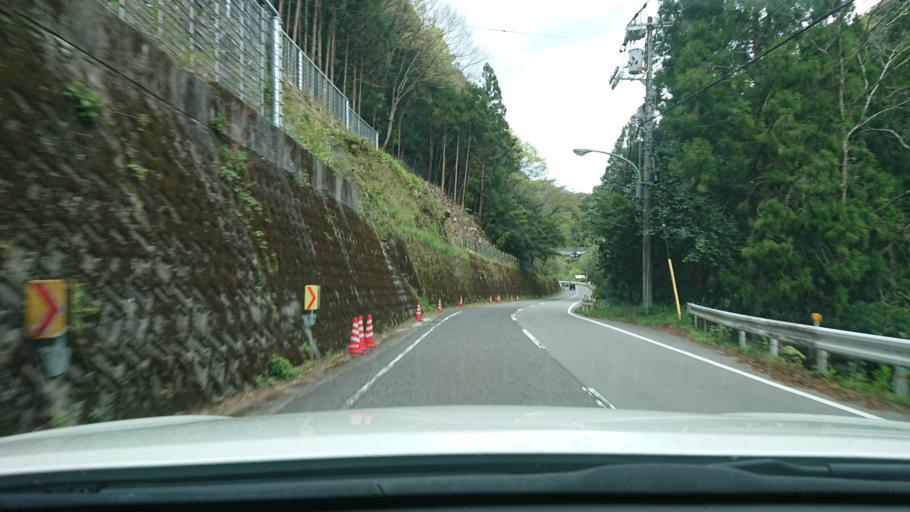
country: JP
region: Tokushima
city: Ishii
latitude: 33.9130
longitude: 134.4203
